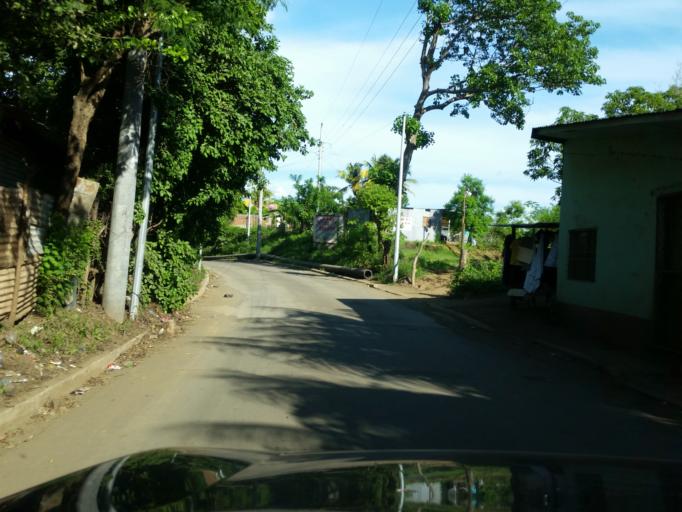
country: NI
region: Managua
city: Managua
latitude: 12.1021
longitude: -86.2185
